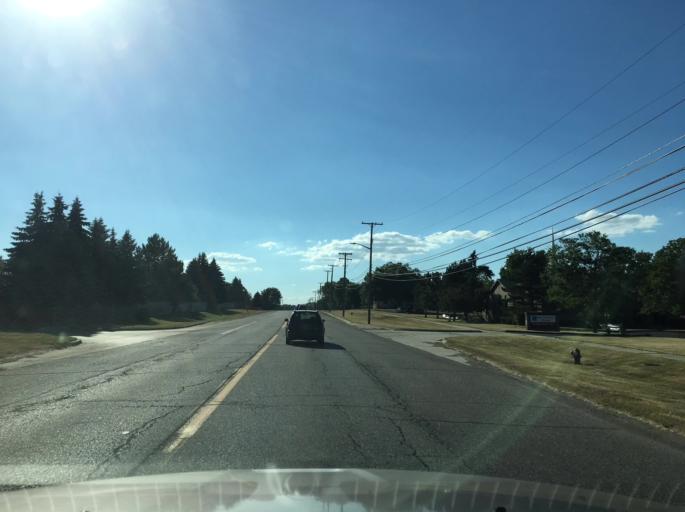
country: US
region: Michigan
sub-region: Macomb County
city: Fraser
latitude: 42.5726
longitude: -82.9786
